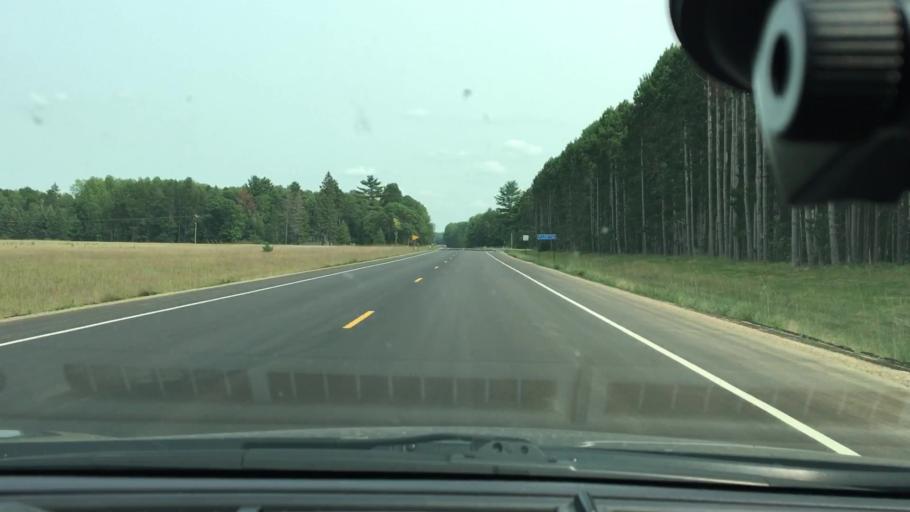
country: US
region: Minnesota
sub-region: Crow Wing County
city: Nisswa
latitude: 46.5293
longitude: -94.2495
